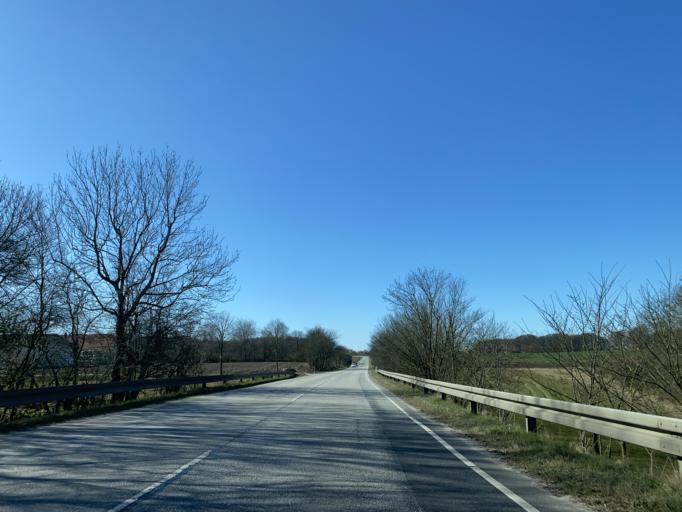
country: DK
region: Central Jutland
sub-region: Randers Kommune
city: Randers
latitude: 56.3976
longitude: 9.9844
